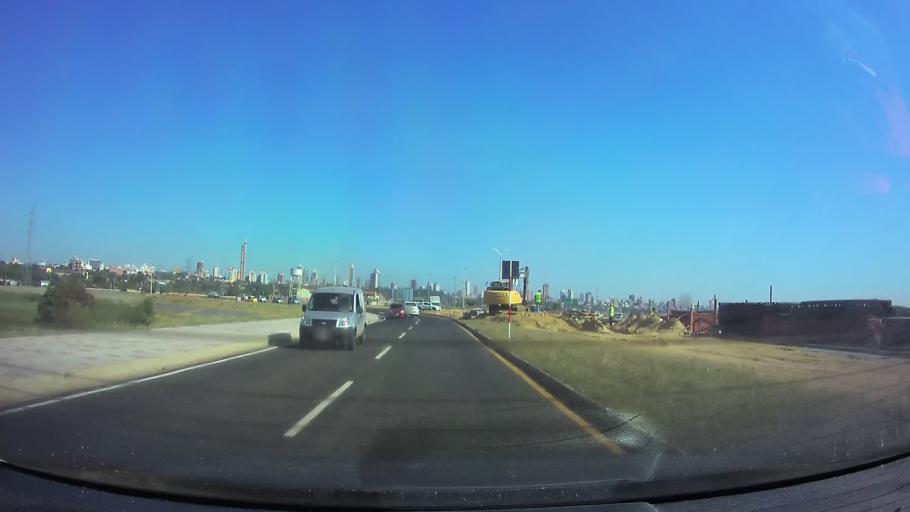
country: PY
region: Asuncion
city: Asuncion
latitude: -25.2693
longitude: -57.6124
